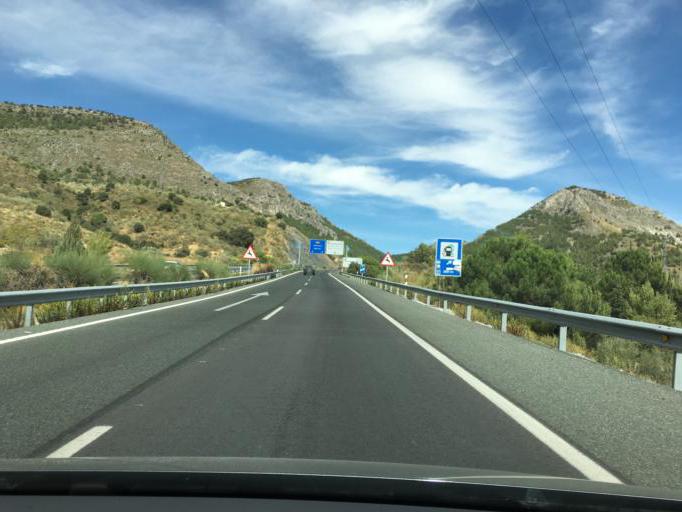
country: ES
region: Andalusia
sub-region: Provincia de Granada
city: Huetor Santillan
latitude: 37.2297
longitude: -3.5020
